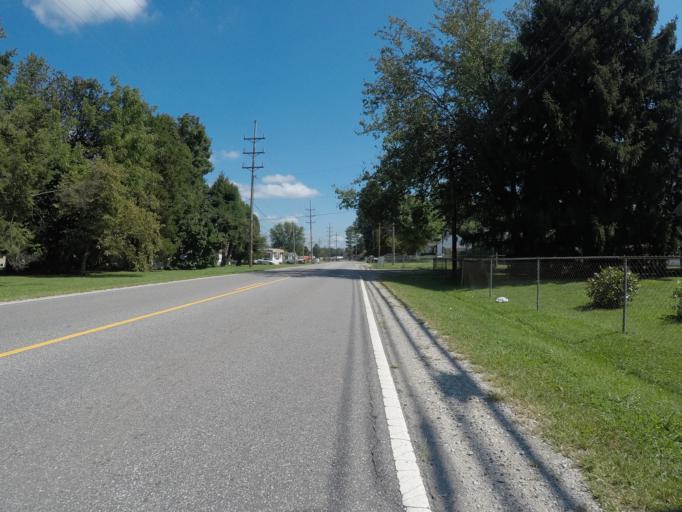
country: US
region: Ohio
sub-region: Lawrence County
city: Burlington
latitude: 38.4093
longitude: -82.5221
